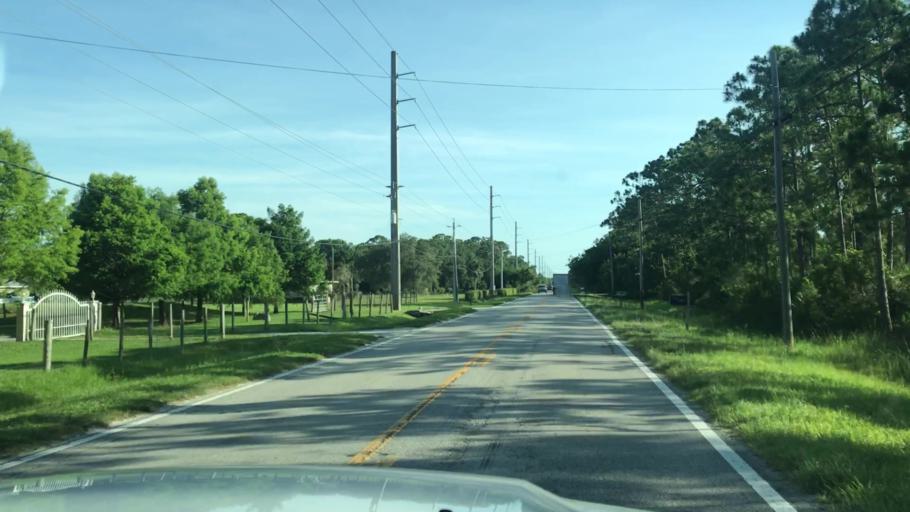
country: US
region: Florida
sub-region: Indian River County
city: Winter Beach
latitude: 27.7132
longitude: -80.4460
